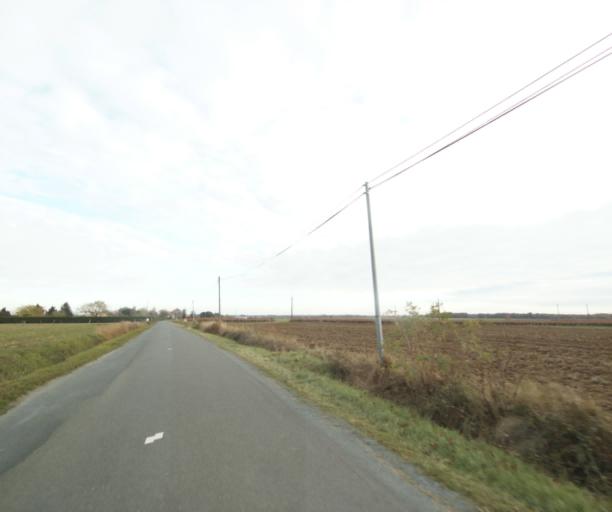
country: FR
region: Poitou-Charentes
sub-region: Departement de la Charente-Maritime
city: Corme-Royal
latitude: 45.7209
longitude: -0.8226
